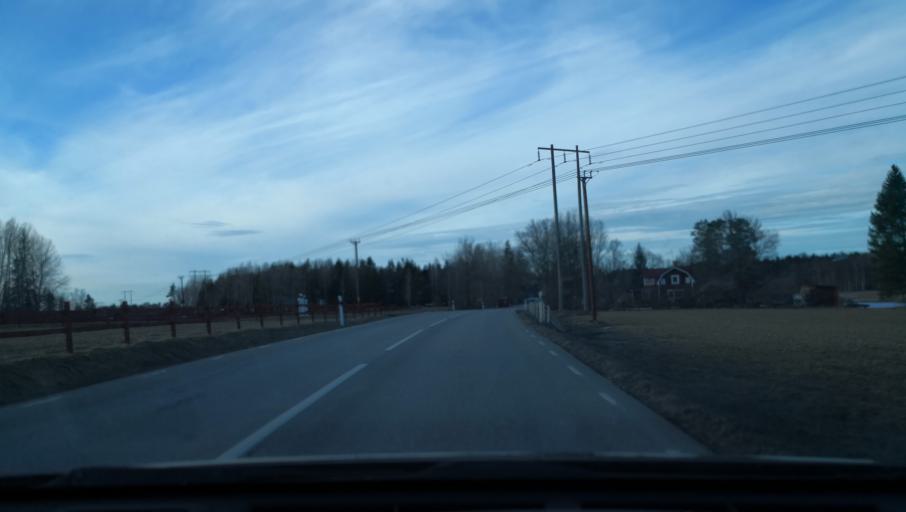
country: SE
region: Uppsala
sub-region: Osthammars Kommun
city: OEsthammar
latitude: 60.3067
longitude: 18.2713
